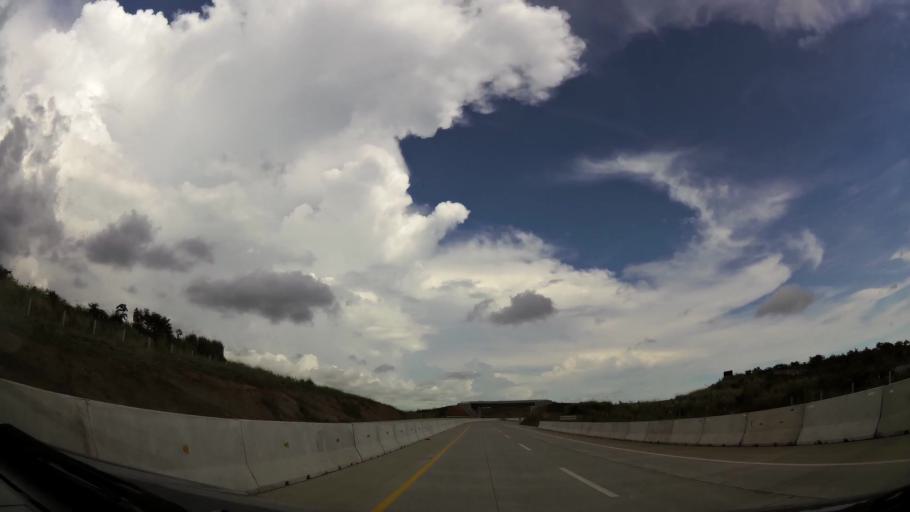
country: PA
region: Panama
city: Tocumen
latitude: 9.1049
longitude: -79.3970
